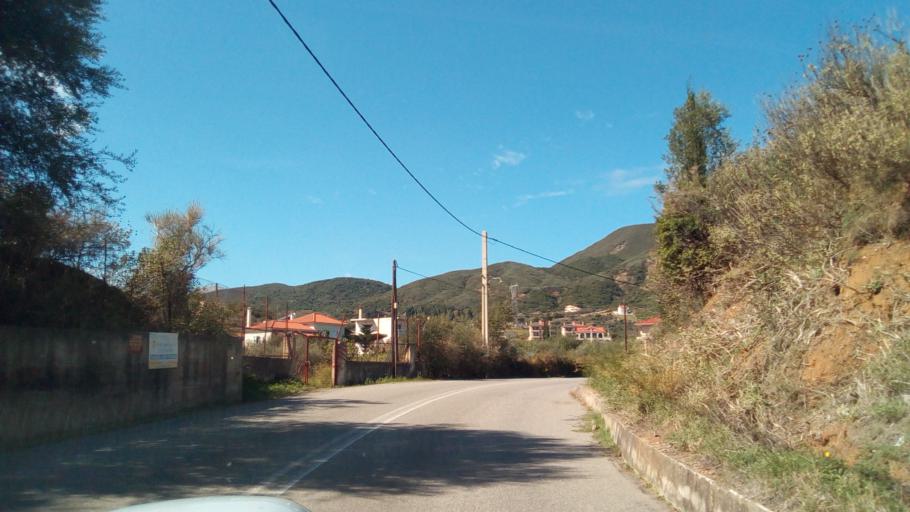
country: GR
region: West Greece
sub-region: Nomos Aitolias kai Akarnanias
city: Antirrio
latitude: 38.3679
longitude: 21.7778
